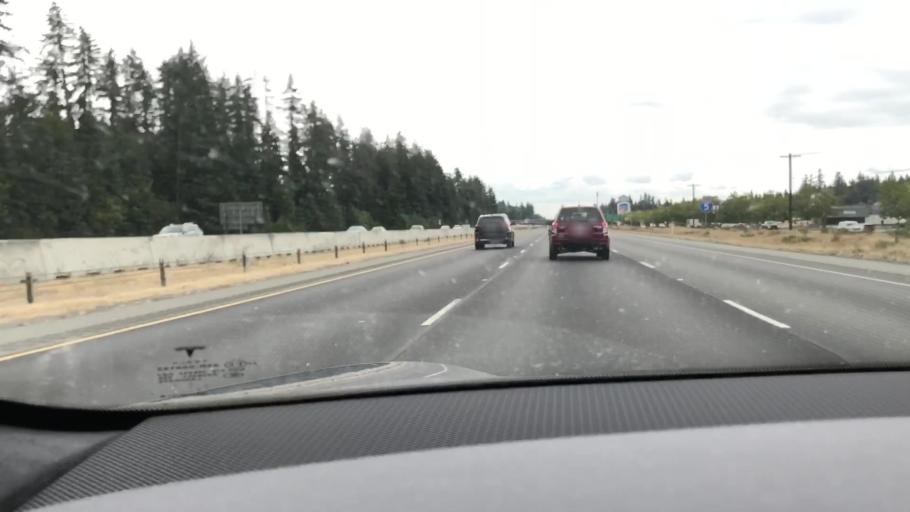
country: US
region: Washington
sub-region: Snohomish County
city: Marysville
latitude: 48.0843
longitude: -122.1850
